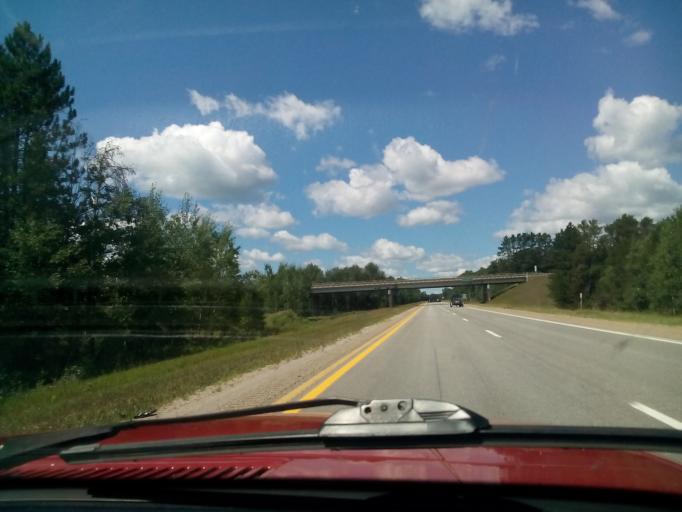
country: US
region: Michigan
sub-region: Roscommon County
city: Roscommon
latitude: 44.4569
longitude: -84.6033
